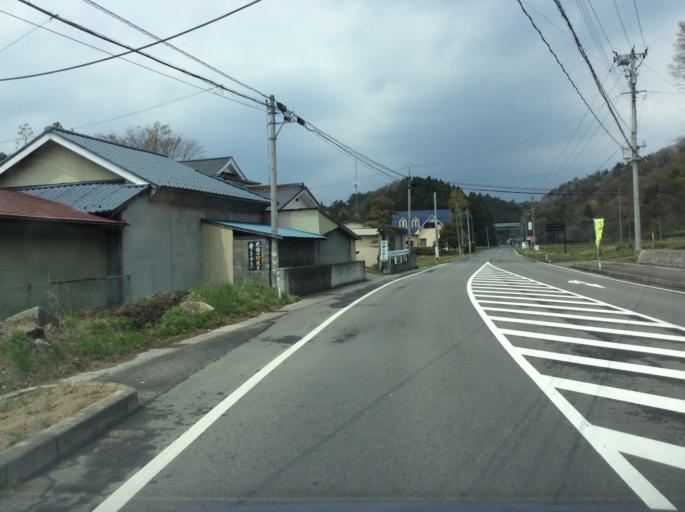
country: JP
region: Fukushima
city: Funehikimachi-funehiki
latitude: 37.3132
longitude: 140.6128
